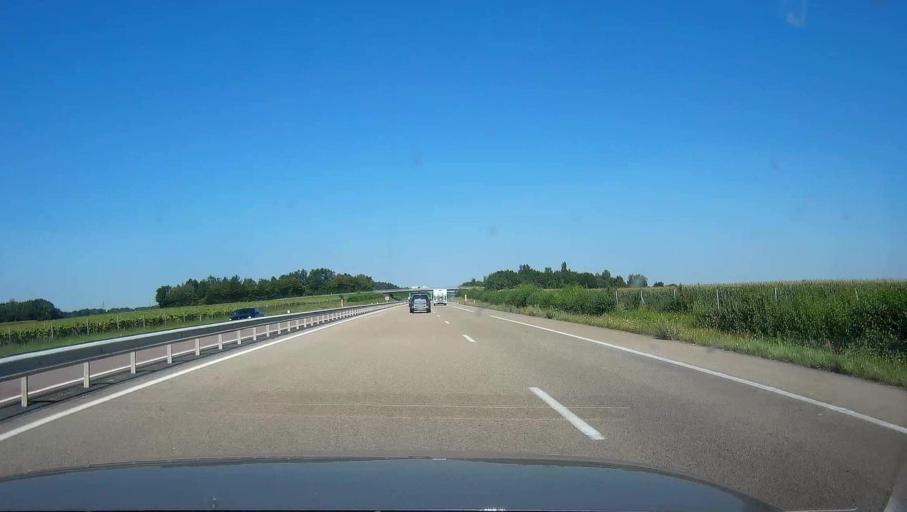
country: FR
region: Champagne-Ardenne
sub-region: Departement de l'Aube
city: Verrieres
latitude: 48.2387
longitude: 4.1726
